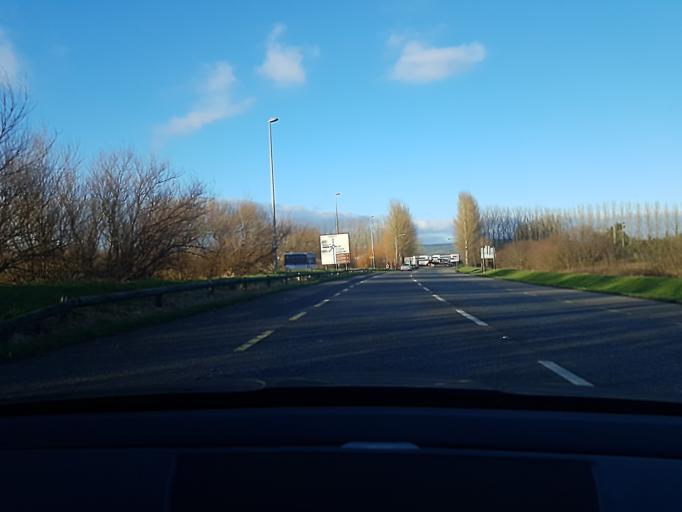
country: IE
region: Munster
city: Moyross
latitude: 52.6717
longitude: -8.6751
